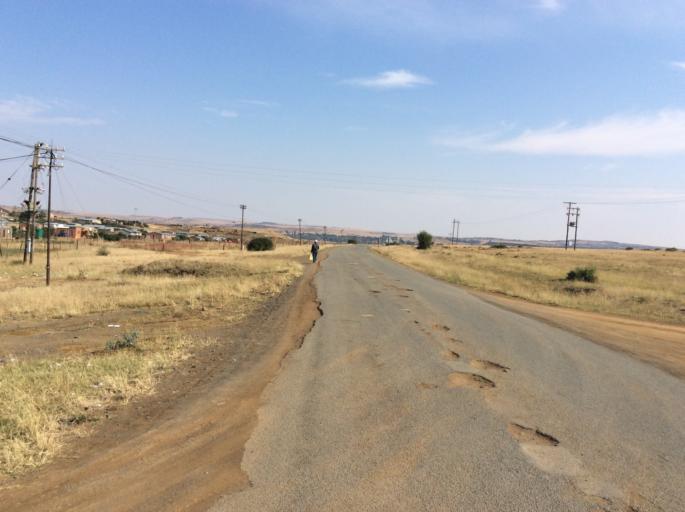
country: LS
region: Mafeteng
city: Mafeteng
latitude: -29.7206
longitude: 27.0117
